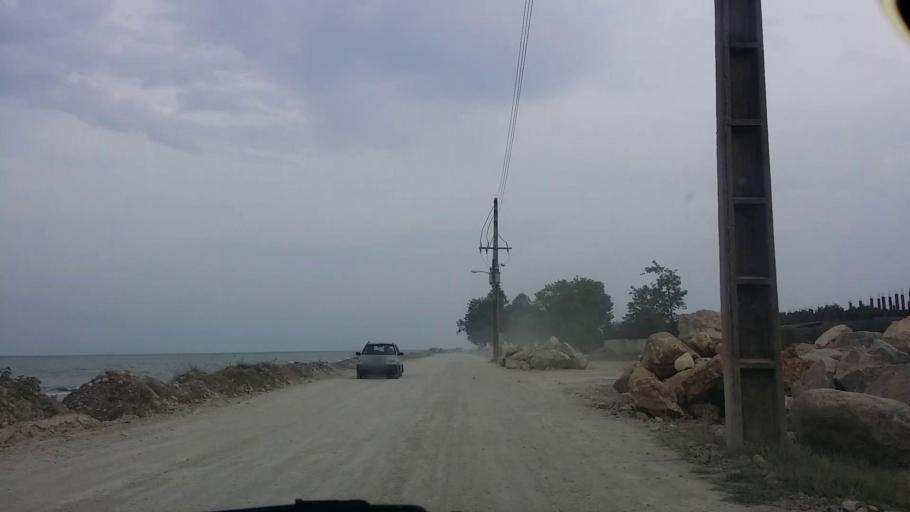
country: IR
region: Mazandaran
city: Chalus
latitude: 36.6854
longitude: 51.4234
